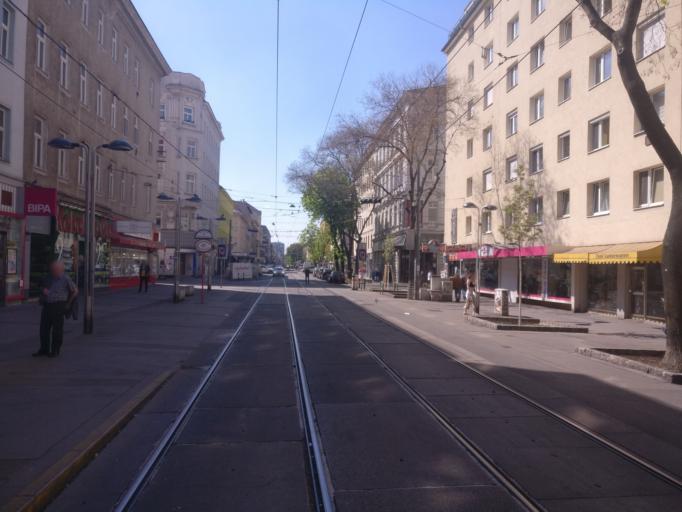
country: AT
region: Vienna
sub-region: Wien Stadt
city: Vienna
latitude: 48.1753
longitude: 16.3770
